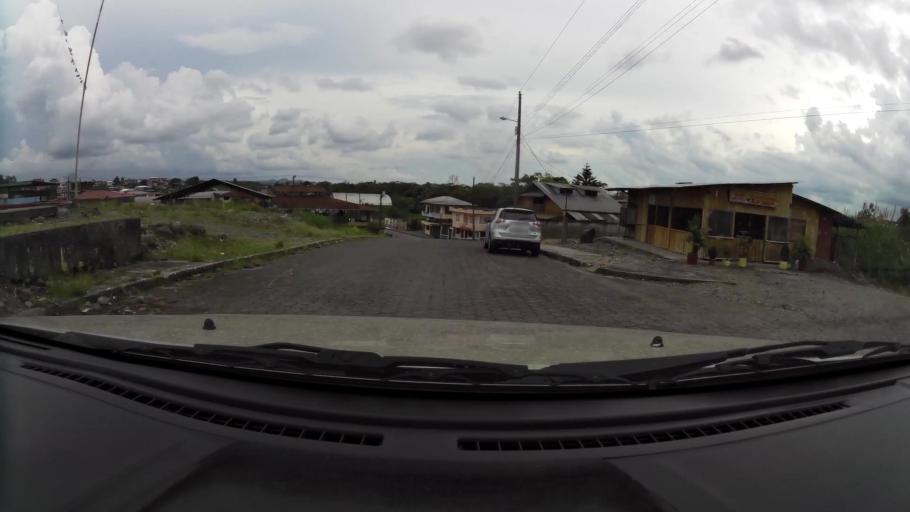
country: EC
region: Pastaza
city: Puyo
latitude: -1.4906
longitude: -78.0081
